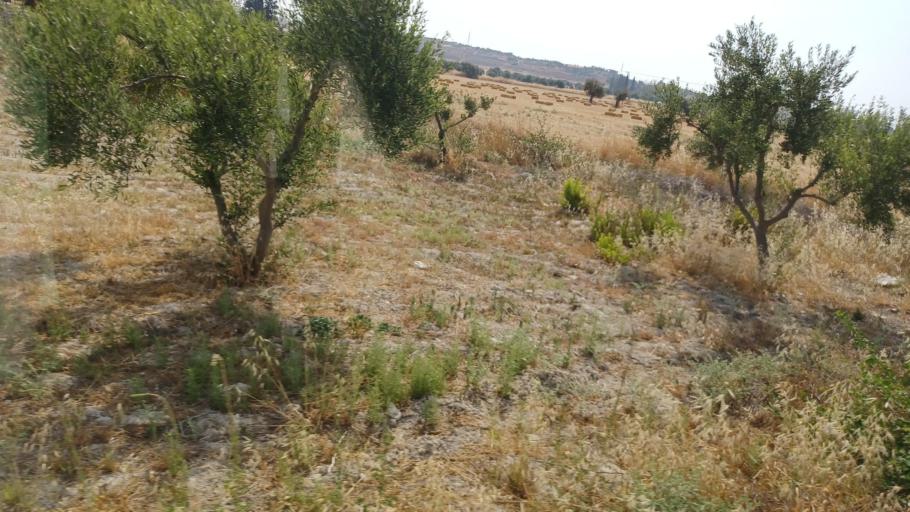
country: CY
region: Larnaka
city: Aradippou
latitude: 34.9248
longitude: 33.5398
